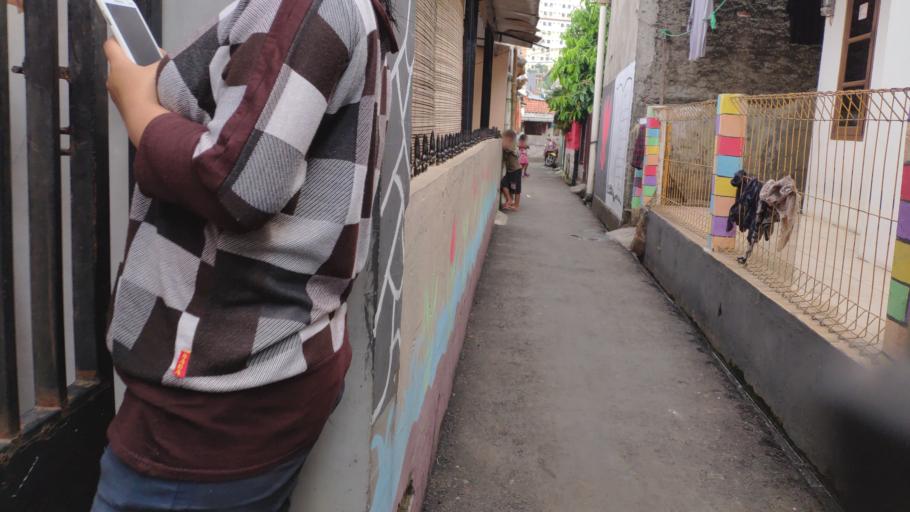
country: ID
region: West Java
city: Depok
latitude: -6.3099
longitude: 106.8346
